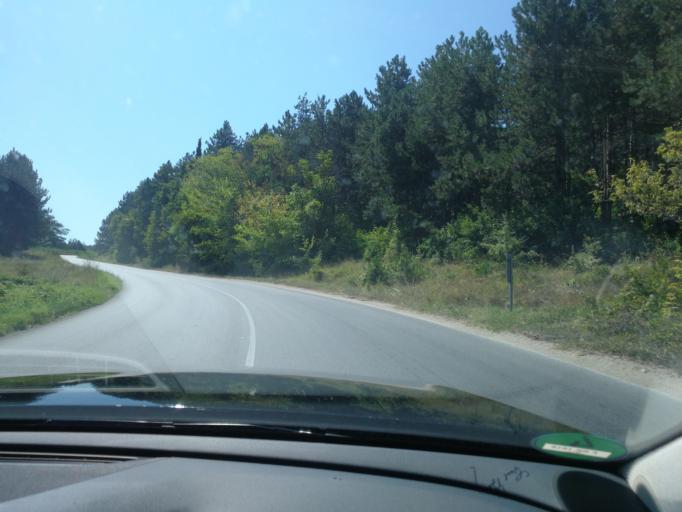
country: BG
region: Khaskovo
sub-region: Obshtina Topolovgrad
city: Topolovgrad
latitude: 42.0819
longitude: 26.3246
